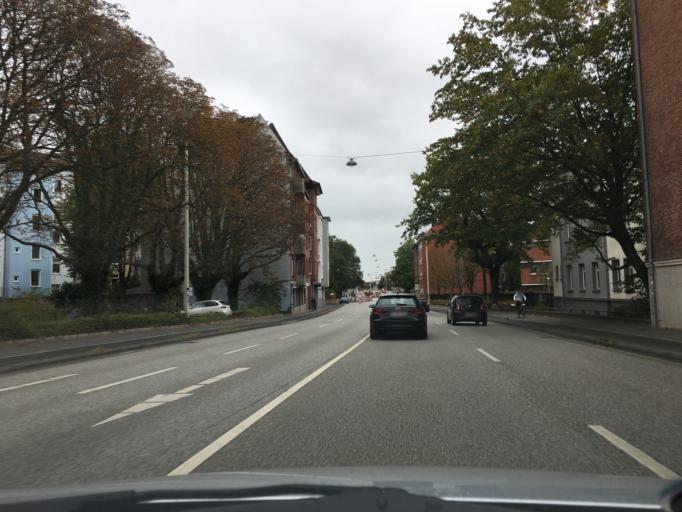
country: DE
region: Schleswig-Holstein
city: Kiel
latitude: 54.3221
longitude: 10.1223
